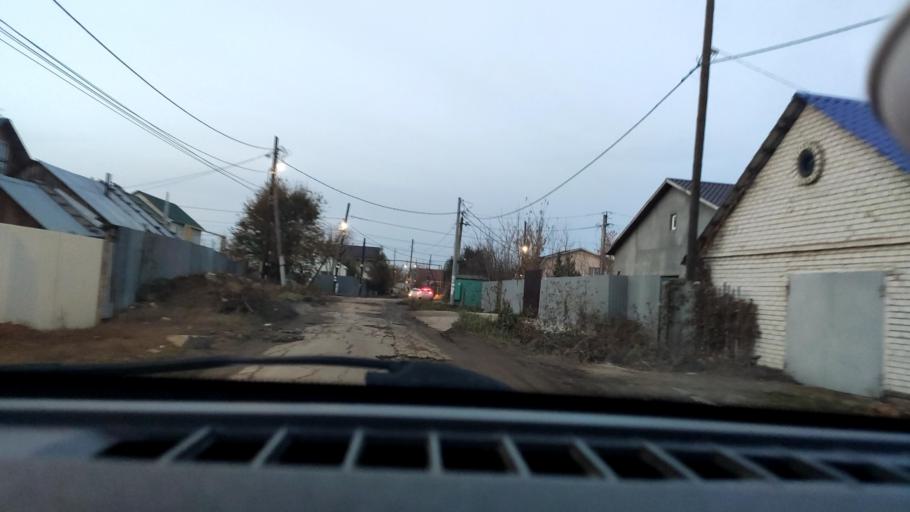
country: RU
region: Samara
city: Samara
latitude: 53.1384
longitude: 50.0960
